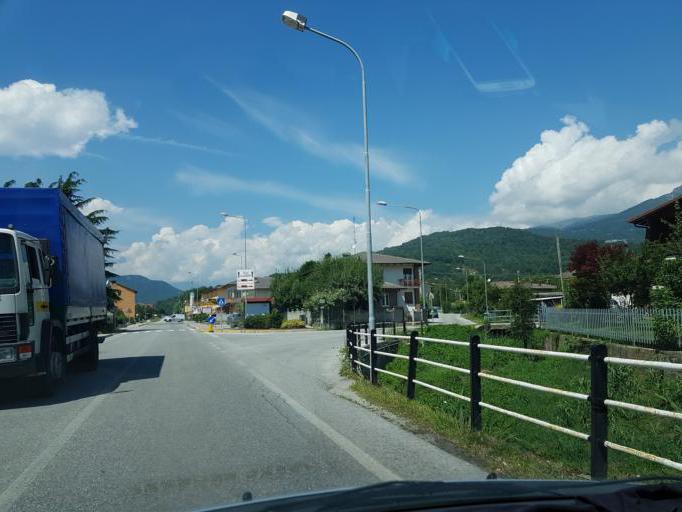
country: IT
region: Piedmont
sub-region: Provincia di Cuneo
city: Tettorosso
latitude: 44.4669
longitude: 7.3402
